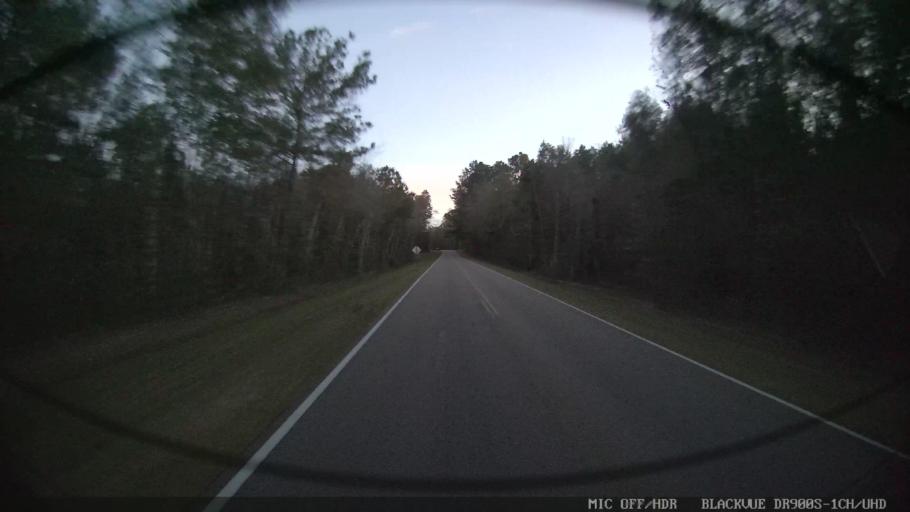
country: US
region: Mississippi
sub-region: Perry County
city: New Augusta
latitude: 31.1094
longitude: -89.1948
